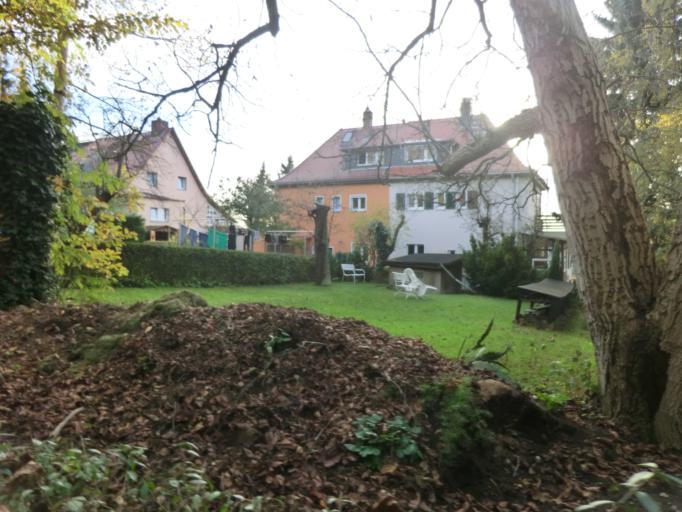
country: DE
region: Saxony
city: Heidenau
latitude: 51.0403
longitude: 13.8423
